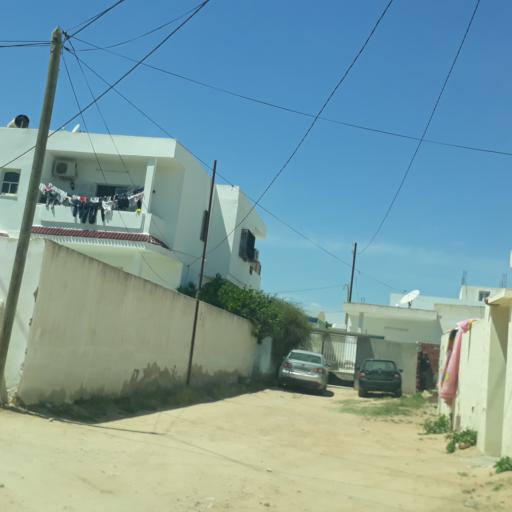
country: TN
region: Safaqis
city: Al Qarmadah
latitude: 34.8062
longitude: 10.7601
